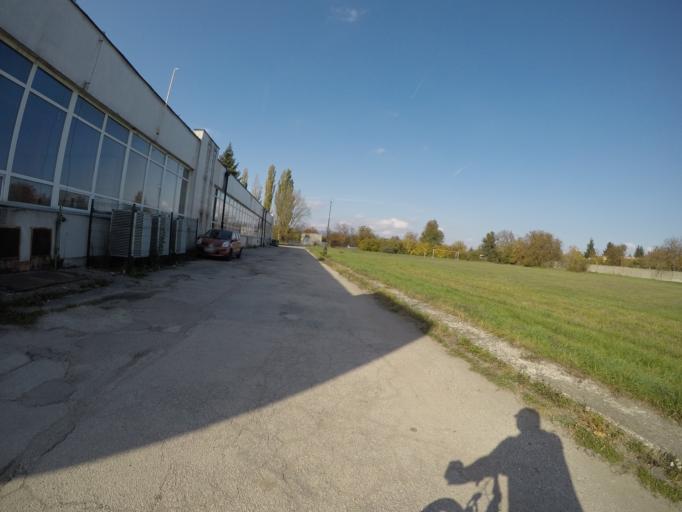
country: SK
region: Trenciansky
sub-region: Okres Nove Mesto nad Vahom
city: Nove Mesto nad Vahom
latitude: 48.7656
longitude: 17.8264
